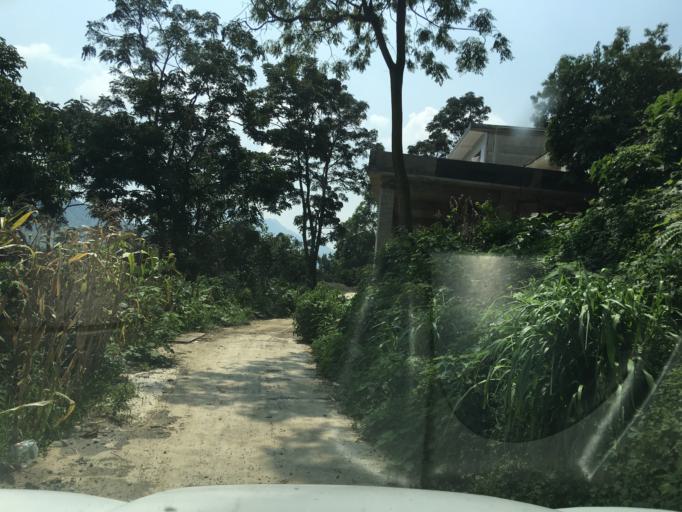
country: CN
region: Guangxi Zhuangzu Zizhiqu
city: Xinzhou
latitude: 24.9949
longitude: 105.7565
